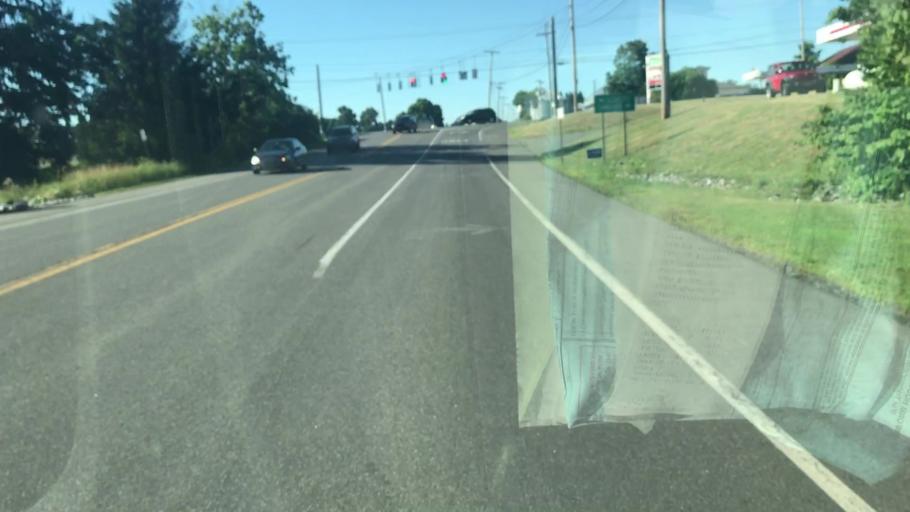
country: US
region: New York
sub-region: Onondaga County
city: Marcellus
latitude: 43.0337
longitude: -76.3650
